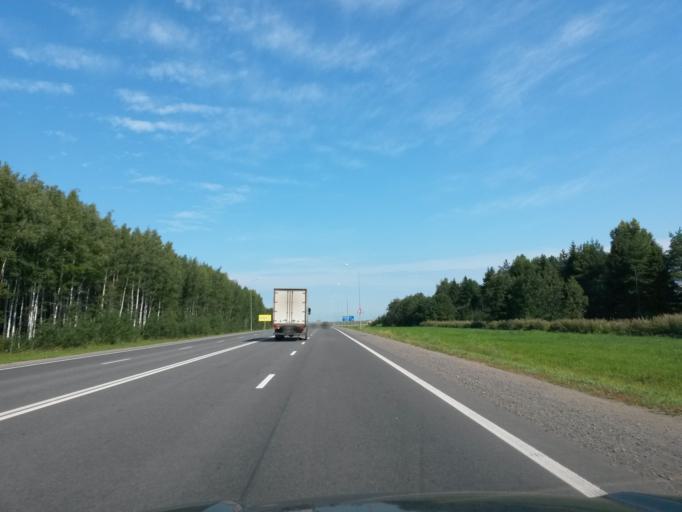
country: RU
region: Jaroslavl
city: Yaroslavl
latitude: 57.7315
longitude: 39.8979
